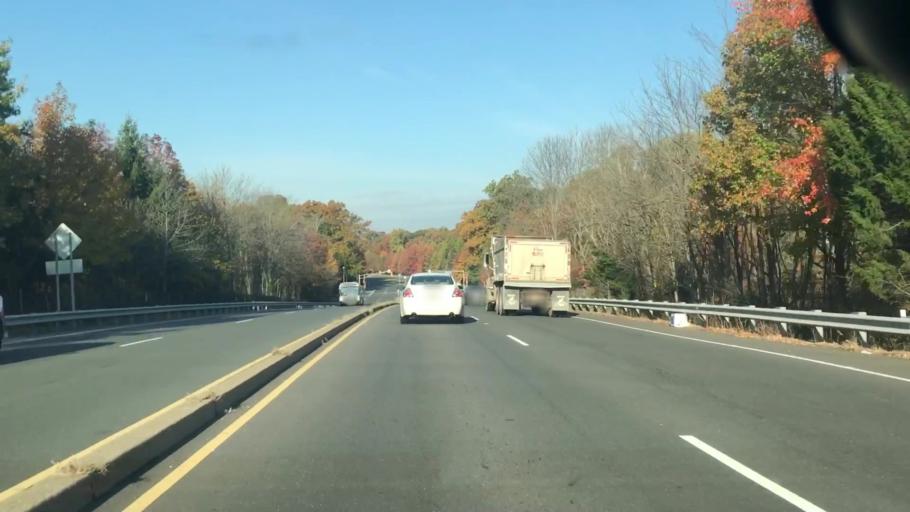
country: US
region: New Jersey
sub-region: Middlesex County
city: Plainsboro Center
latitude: 40.3390
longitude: -74.5959
